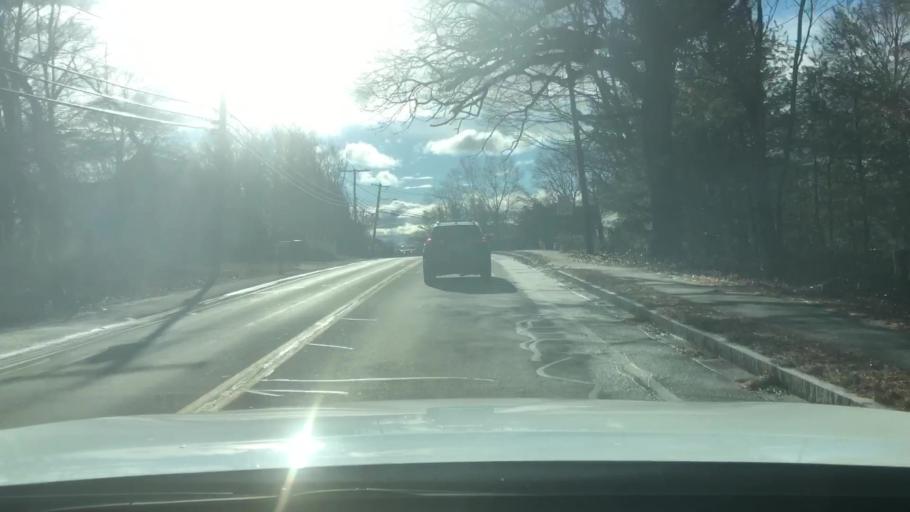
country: US
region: Massachusetts
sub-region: Norfolk County
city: Bellingham
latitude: 42.0563
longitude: -71.4851
